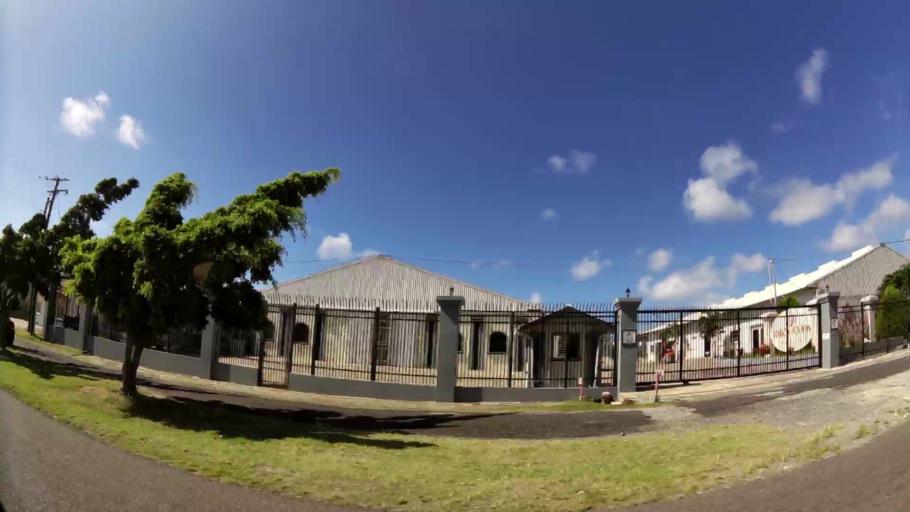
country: LC
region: Laborie Quarter
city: Laborie
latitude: 13.7411
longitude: -60.9709
